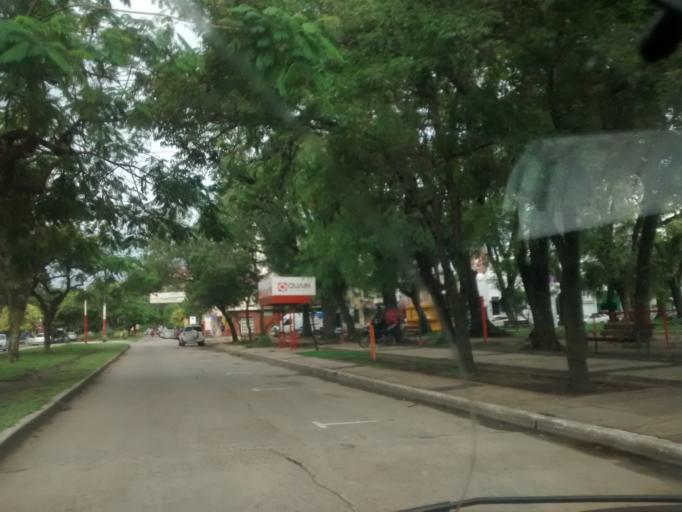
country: AR
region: Chaco
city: Resistencia
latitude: -27.4508
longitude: -58.9947
